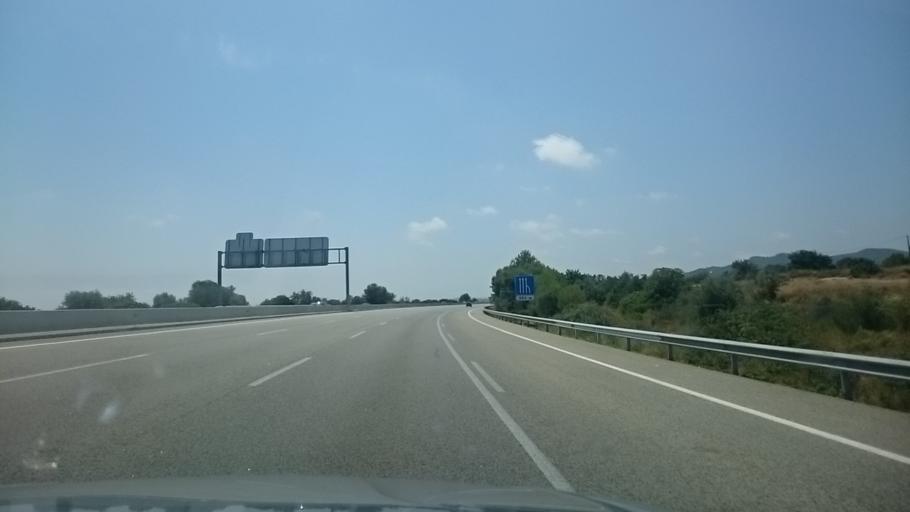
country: ES
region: Catalonia
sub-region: Provincia de Tarragona
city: Santa Oliva
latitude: 41.2579
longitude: 1.5392
